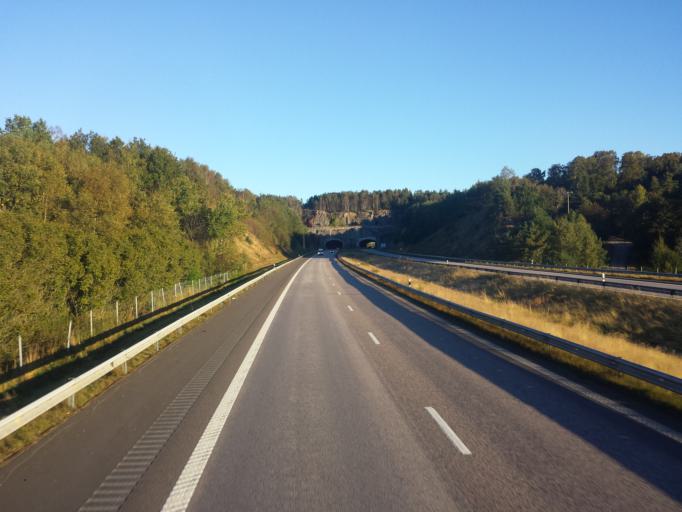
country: SE
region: Halland
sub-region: Varbergs Kommun
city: Veddige
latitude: 57.2314
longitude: 12.2262
